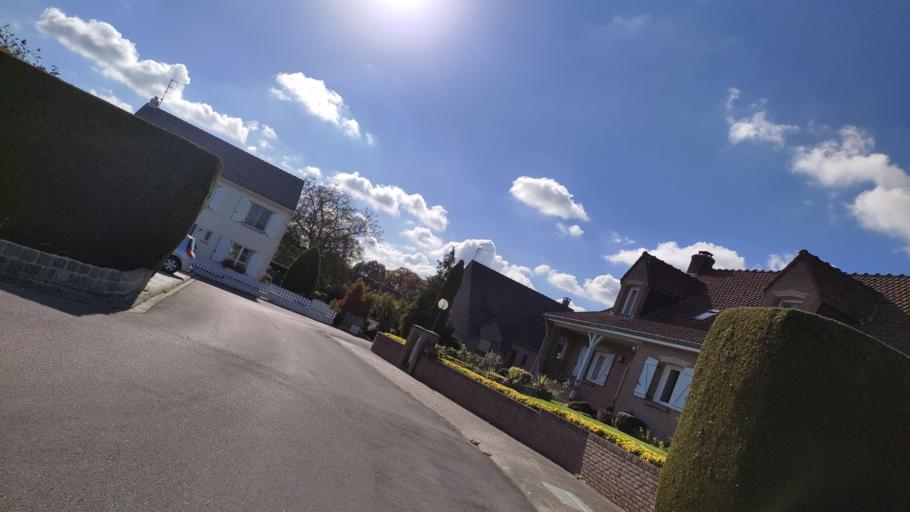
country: FR
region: Nord-Pas-de-Calais
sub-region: Departement du Pas-de-Calais
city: Sainte-Catherine
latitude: 50.3066
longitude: 2.7682
